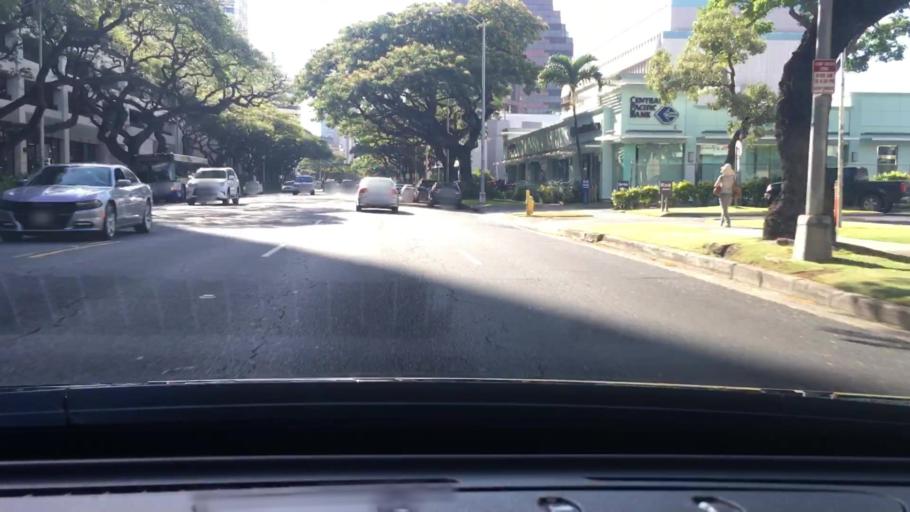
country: US
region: Hawaii
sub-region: Honolulu County
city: Honolulu
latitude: 21.2923
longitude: -157.8405
